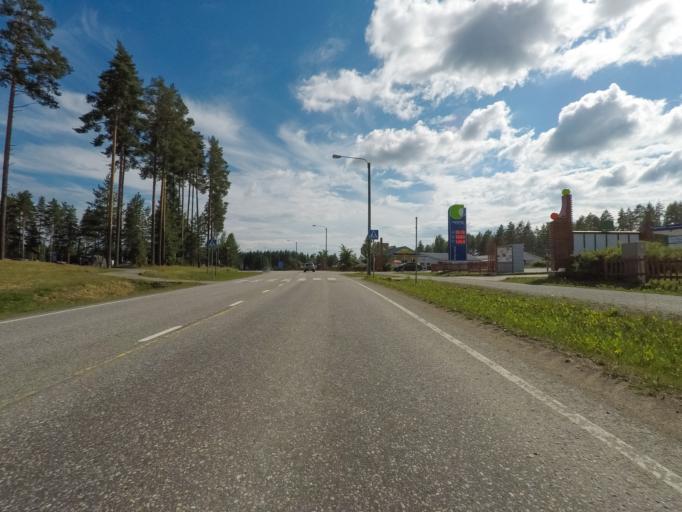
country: FI
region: Southern Savonia
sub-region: Mikkeli
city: Pertunmaa
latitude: 61.4215
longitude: 26.4334
